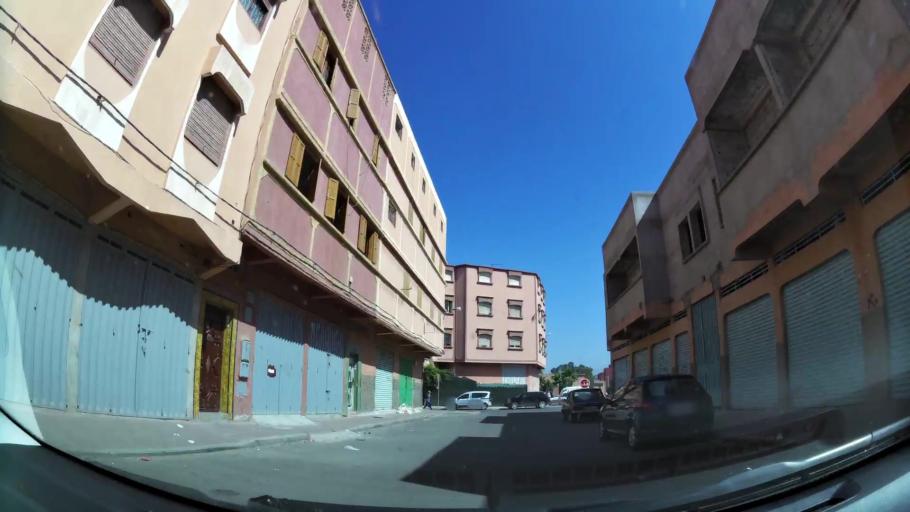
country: MA
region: Souss-Massa-Draa
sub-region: Inezgane-Ait Mellou
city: Inezgane
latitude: 30.3434
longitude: -9.5038
